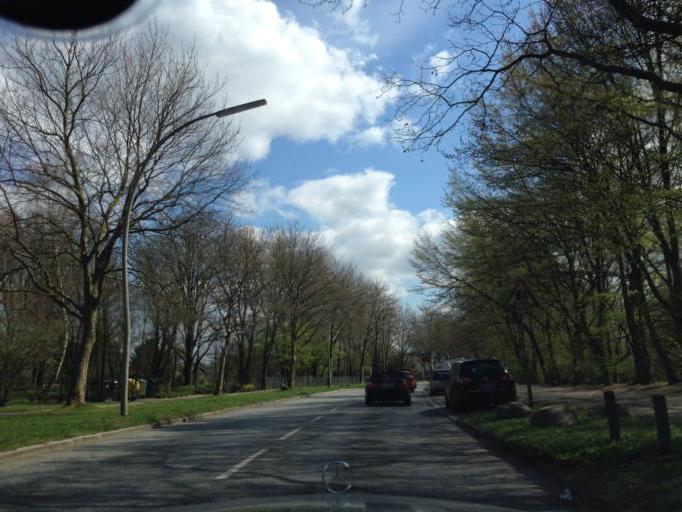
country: DE
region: Hamburg
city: Wandsbek
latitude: 53.5590
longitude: 10.1096
